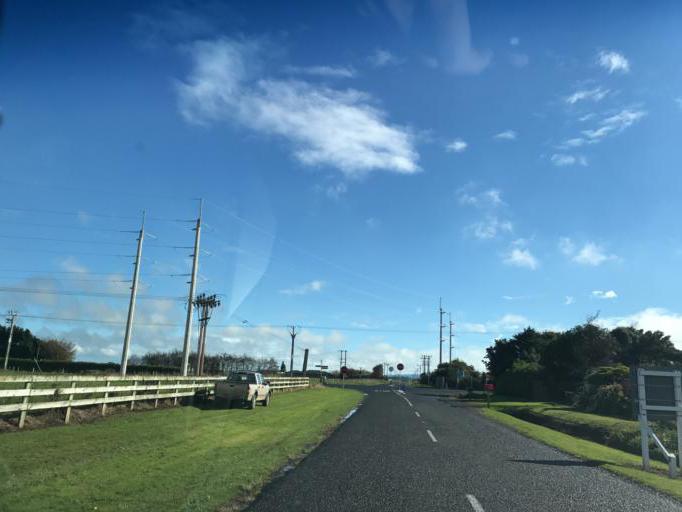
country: NZ
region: Taranaki
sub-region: South Taranaki District
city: Hawera
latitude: -39.5679
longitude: 174.3105
